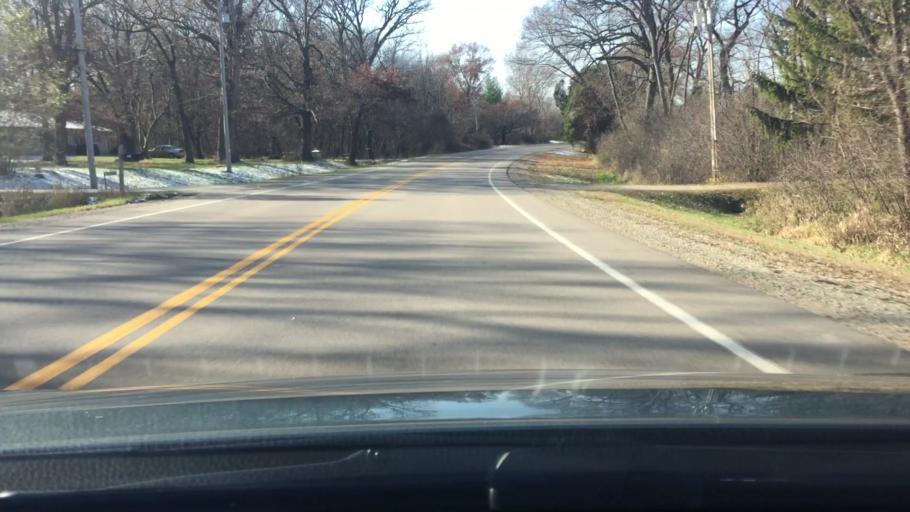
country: US
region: Wisconsin
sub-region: Jefferson County
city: Cambridge
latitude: 43.0092
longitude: -89.0032
